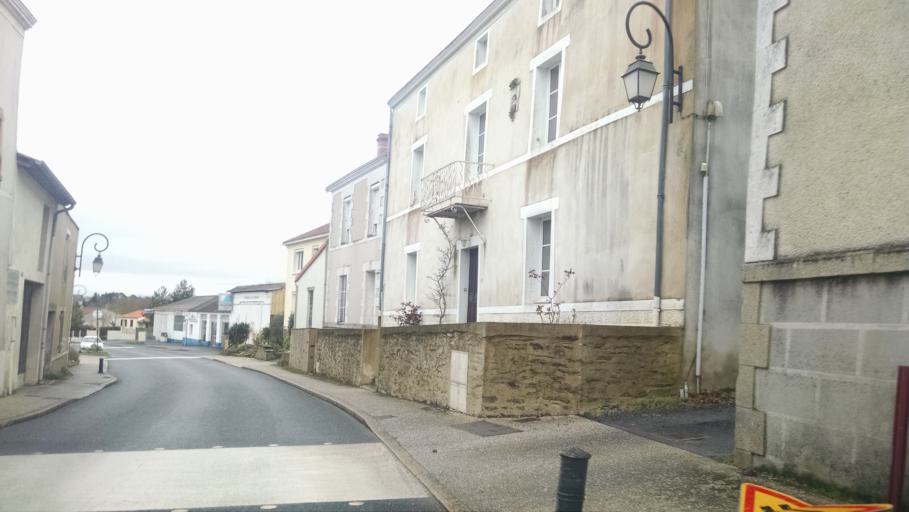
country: FR
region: Pays de la Loire
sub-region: Departement de la Loire-Atlantique
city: Monnieres
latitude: 47.1328
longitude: -1.3540
